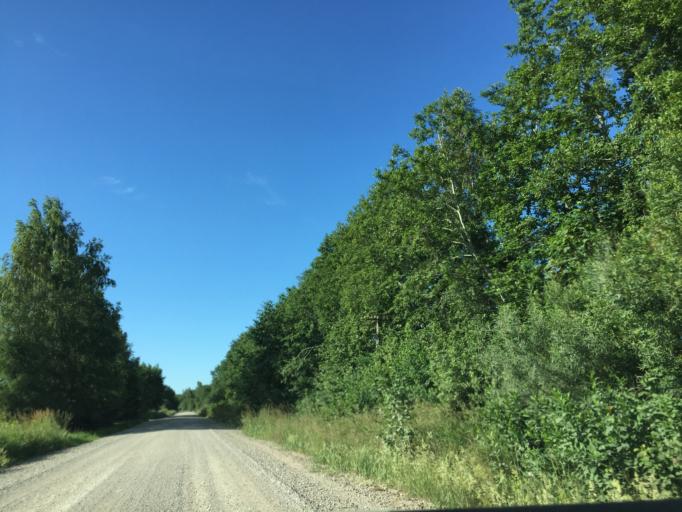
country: LV
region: Ventspils Rajons
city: Piltene
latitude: 57.3203
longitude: 21.6893
